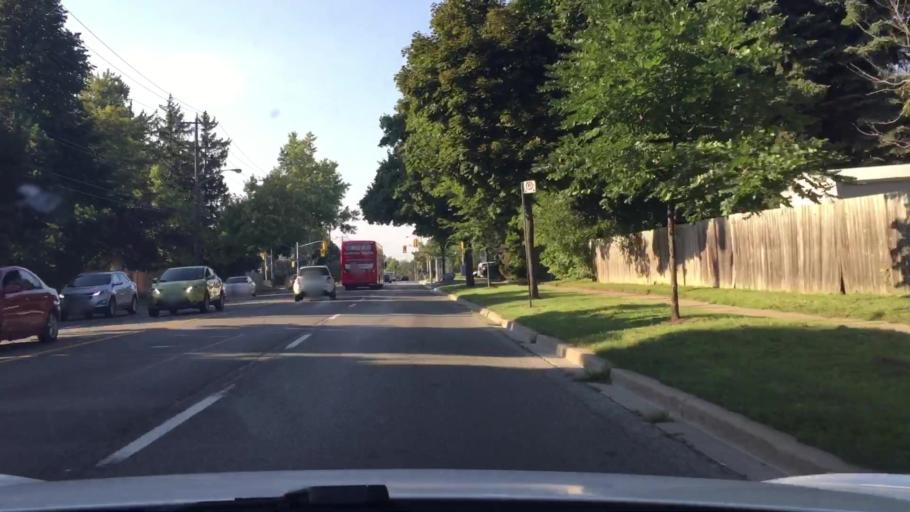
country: CA
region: Ontario
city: Scarborough
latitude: 43.7960
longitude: -79.3046
